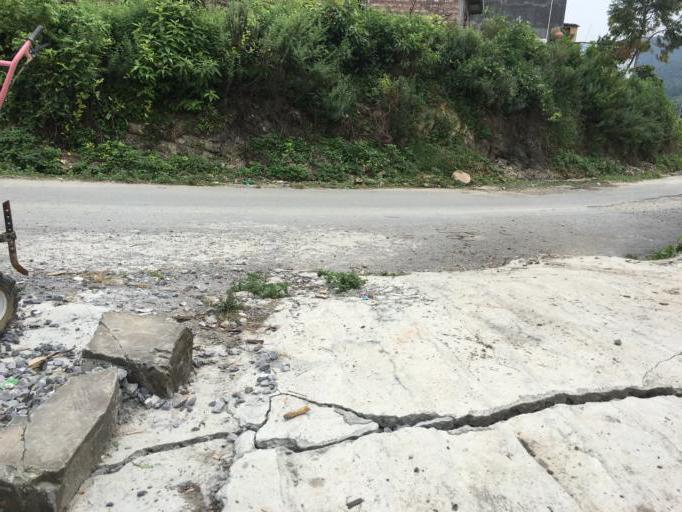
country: CN
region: Guangxi Zhuangzu Zizhiqu
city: Tongle
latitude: 25.1199
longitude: 106.4234
